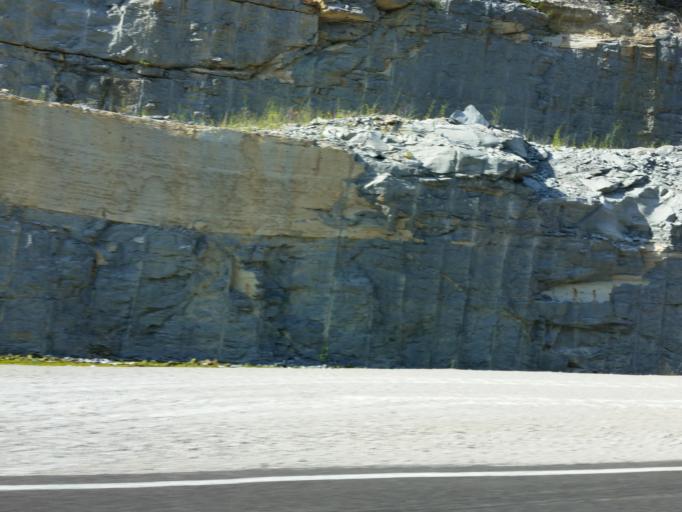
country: US
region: Tennessee
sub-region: Maury County
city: Mount Pleasant
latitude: 35.5688
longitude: -87.3379
